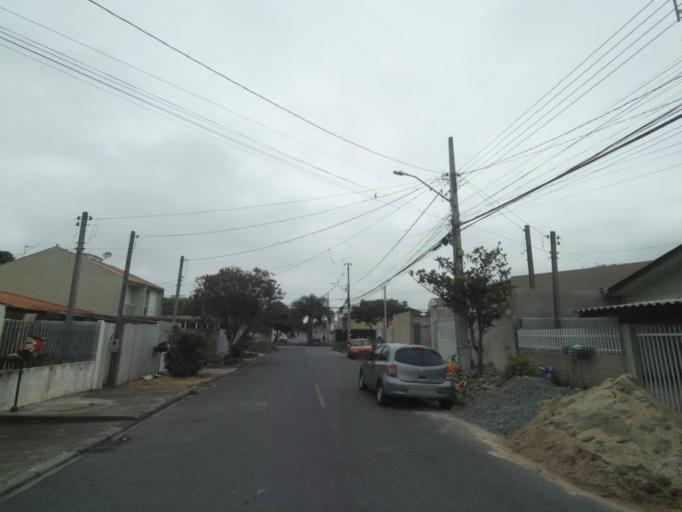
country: BR
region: Parana
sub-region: Araucaria
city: Araucaria
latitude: -25.5462
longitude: -49.3406
